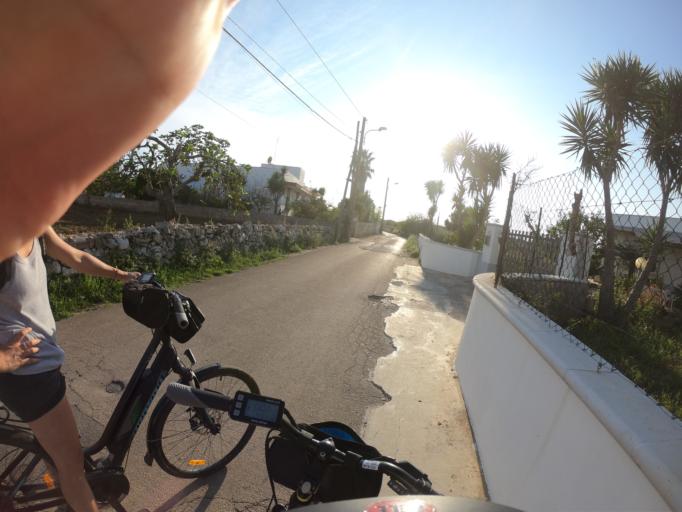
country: IT
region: Apulia
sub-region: Provincia di Lecce
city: Montesardo
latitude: 39.8787
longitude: 18.3361
